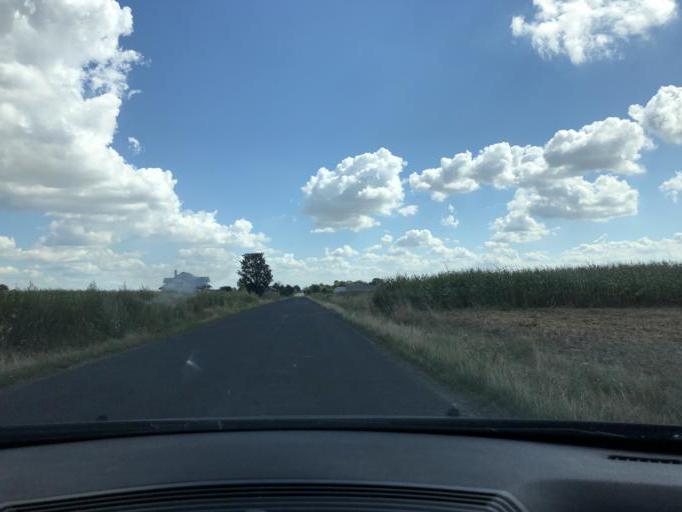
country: PL
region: Lodz Voivodeship
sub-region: Powiat wieruszowski
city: Walichnowy
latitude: 51.2612
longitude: 18.3745
